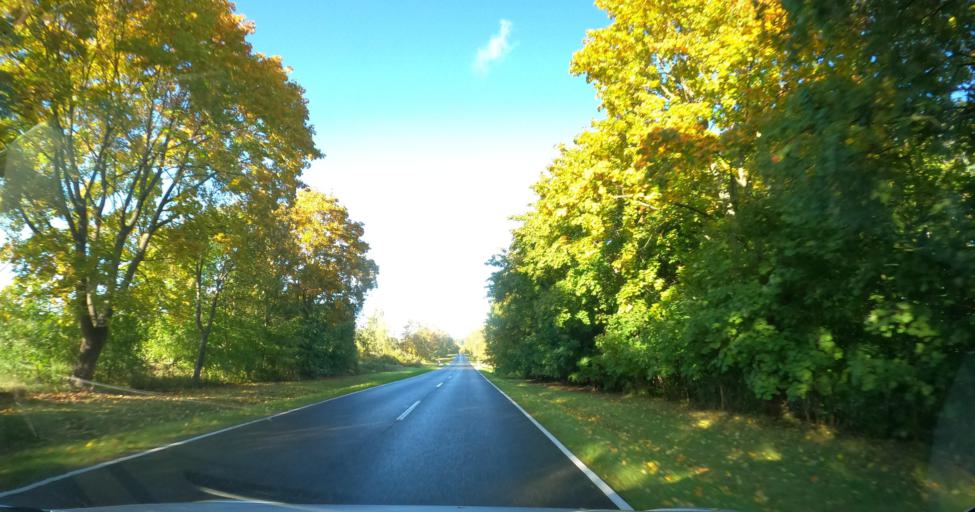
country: PL
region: Lubusz
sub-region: Powiat zielonogorski
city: Zabor
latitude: 51.9411
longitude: 15.6667
